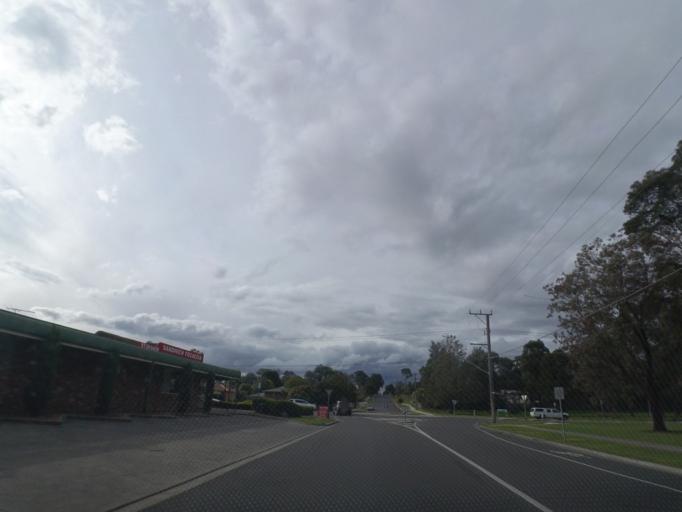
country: AU
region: Victoria
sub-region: Yarra Ranges
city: Lilydale
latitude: -37.7510
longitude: 145.3441
